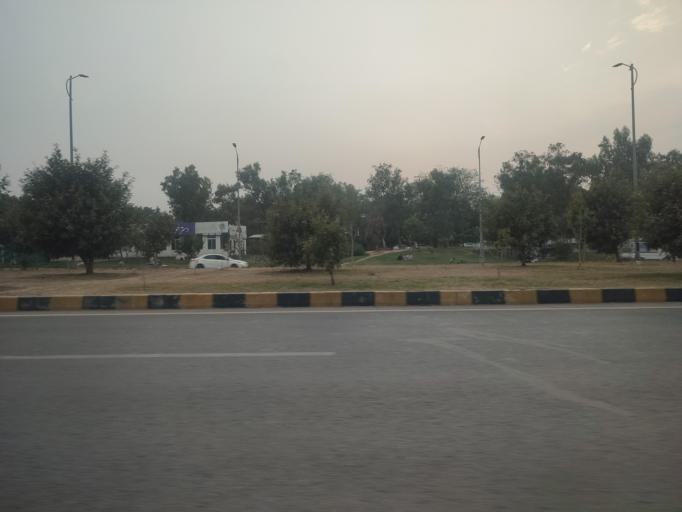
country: PK
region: Islamabad
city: Islamabad
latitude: 33.6868
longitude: 73.0461
